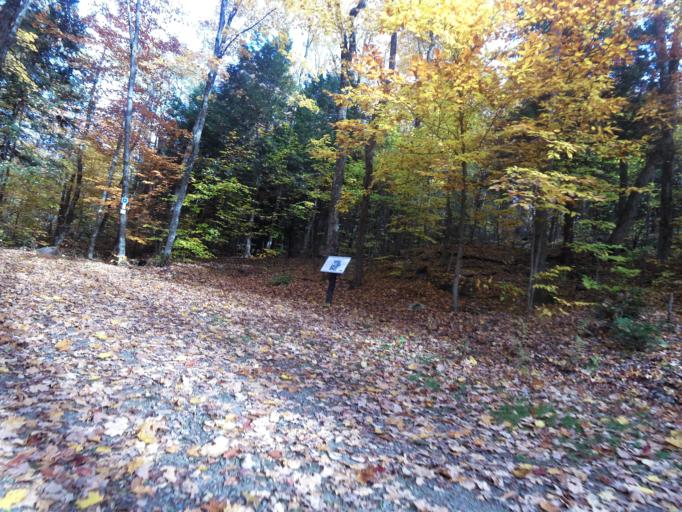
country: CA
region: Quebec
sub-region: Outaouais
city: Gatineau
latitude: 45.4999
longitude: -75.8604
